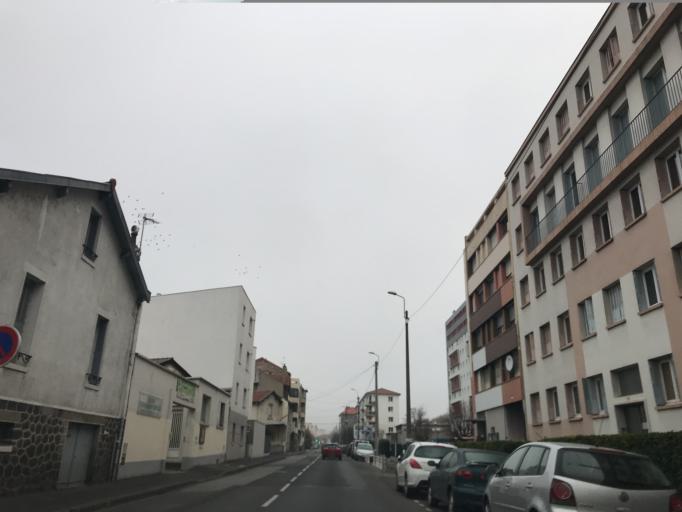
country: FR
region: Auvergne
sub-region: Departement du Puy-de-Dome
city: Clermont-Ferrand
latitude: 45.7803
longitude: 3.1083
